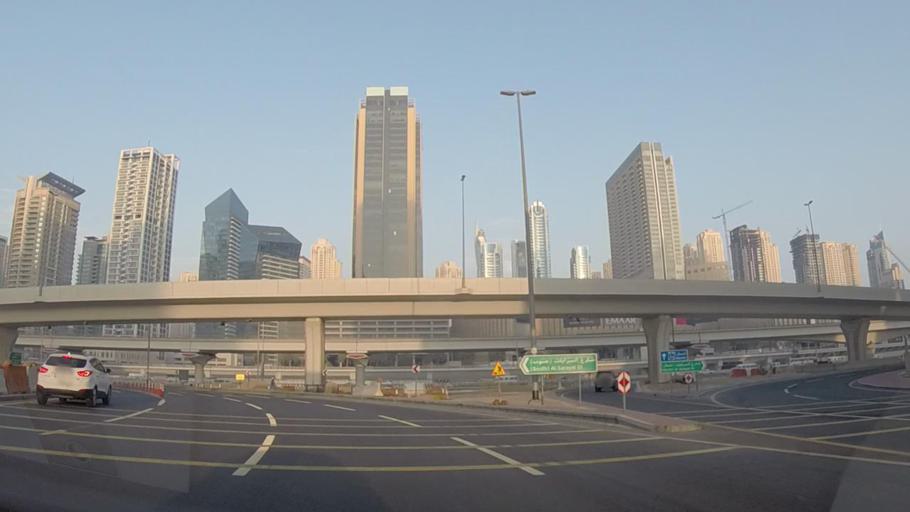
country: AE
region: Dubai
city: Dubai
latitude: 25.0738
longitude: 55.1426
